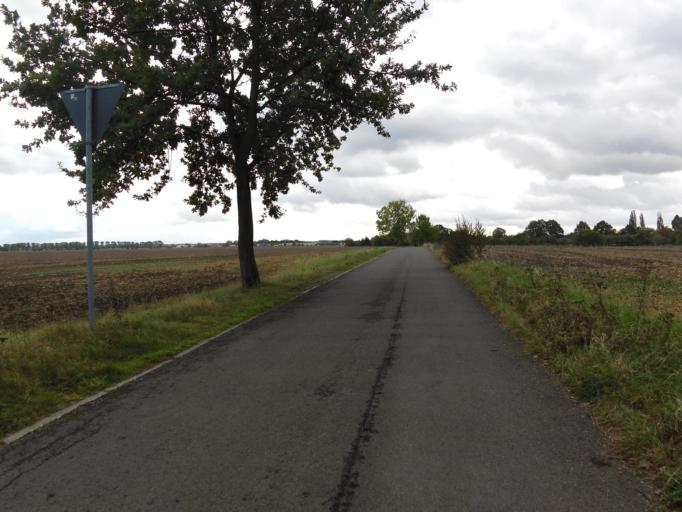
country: DE
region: Saxony
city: Borsdorf
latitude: 51.3348
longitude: 12.4895
